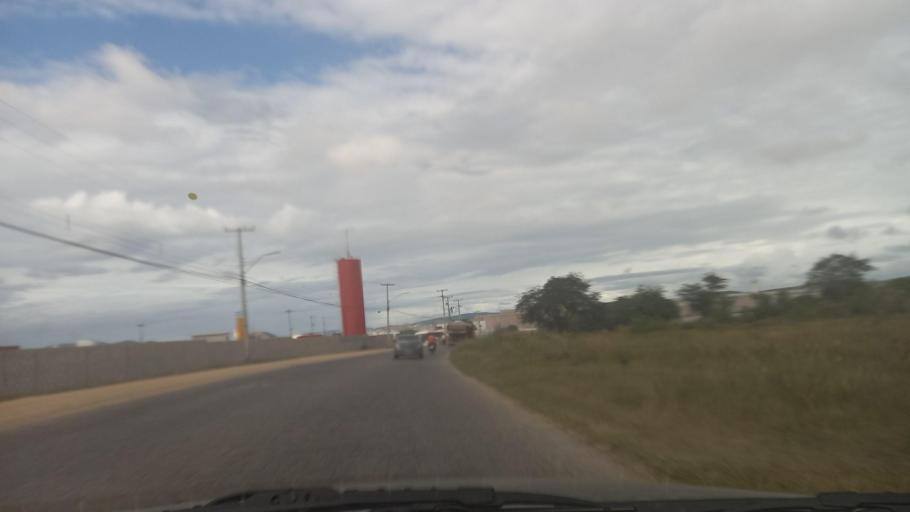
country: BR
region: Pernambuco
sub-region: Caruaru
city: Caruaru
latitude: -8.2895
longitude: -36.0211
